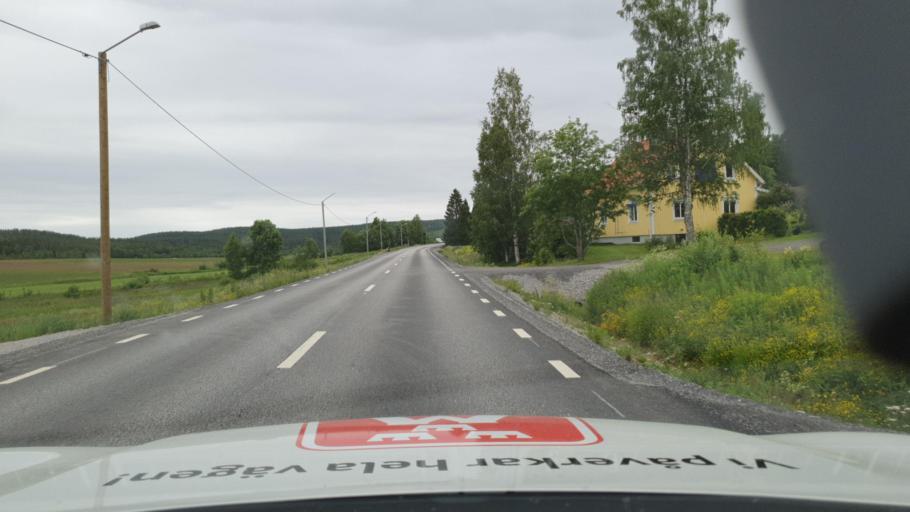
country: SE
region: Vaesterbotten
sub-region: Vannas Kommun
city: Vaennaes
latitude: 63.7423
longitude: 19.6508
